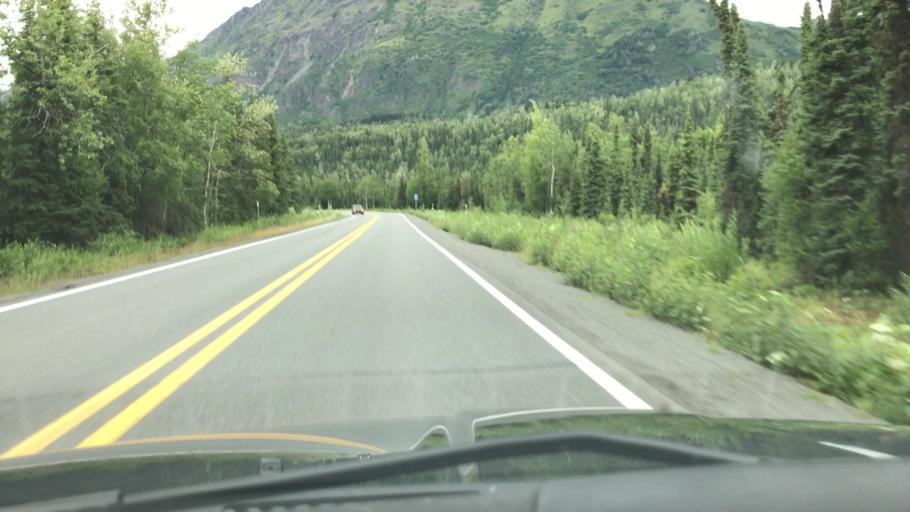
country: US
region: Alaska
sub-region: Kenai Peninsula Borough
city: Seward
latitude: 60.4850
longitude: -149.9614
